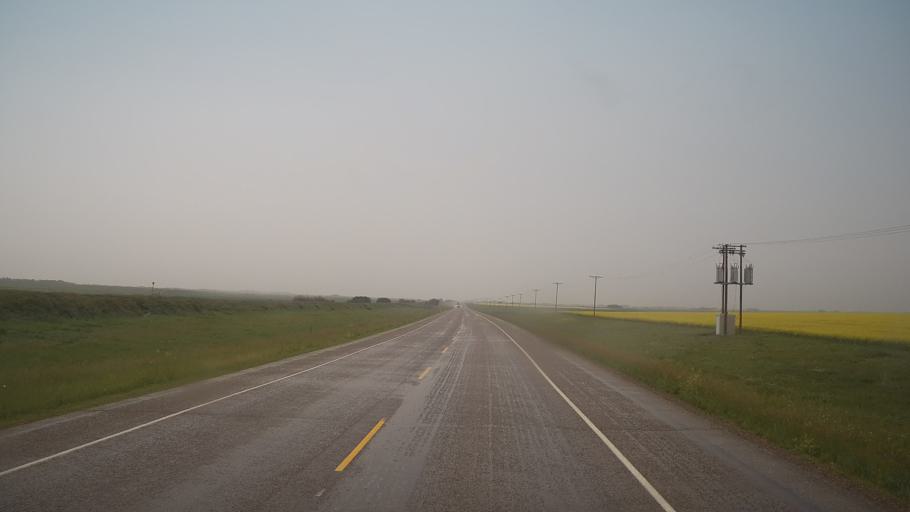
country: CA
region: Saskatchewan
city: Biggar
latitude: 52.1440
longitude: -108.2005
